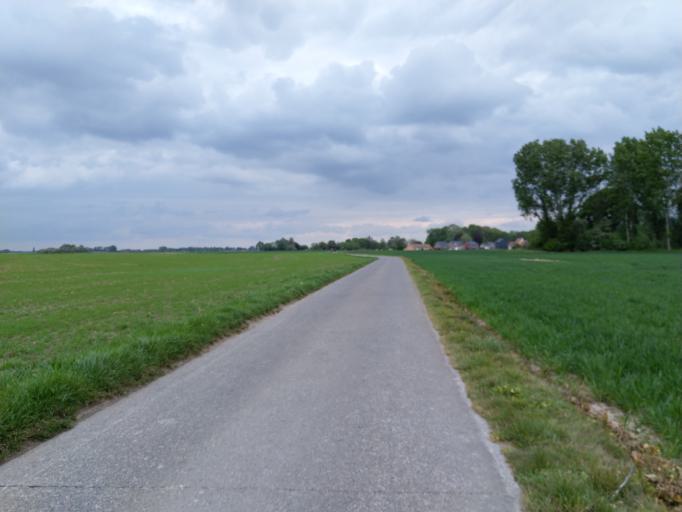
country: BE
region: Wallonia
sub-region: Province du Hainaut
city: Jurbise
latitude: 50.5136
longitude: 3.8837
